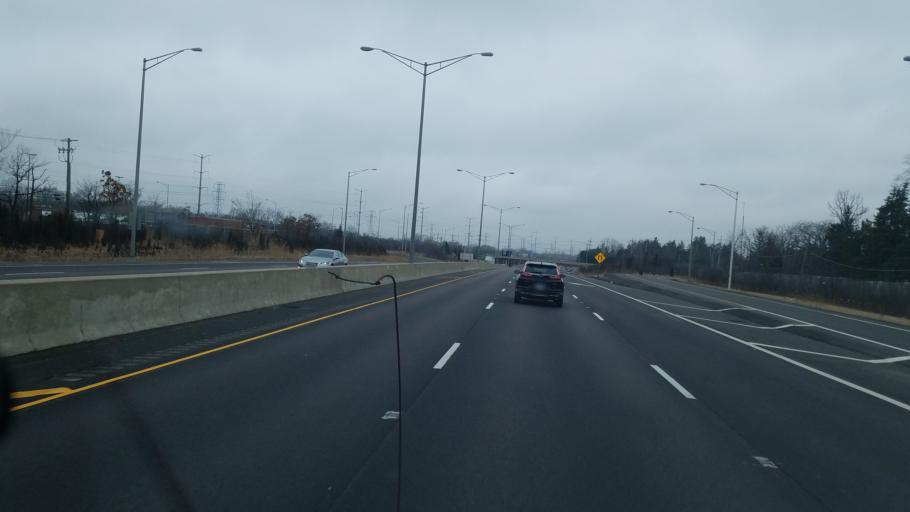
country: US
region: Illinois
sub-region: Lake County
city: Highland Park
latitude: 42.1574
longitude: -87.8031
